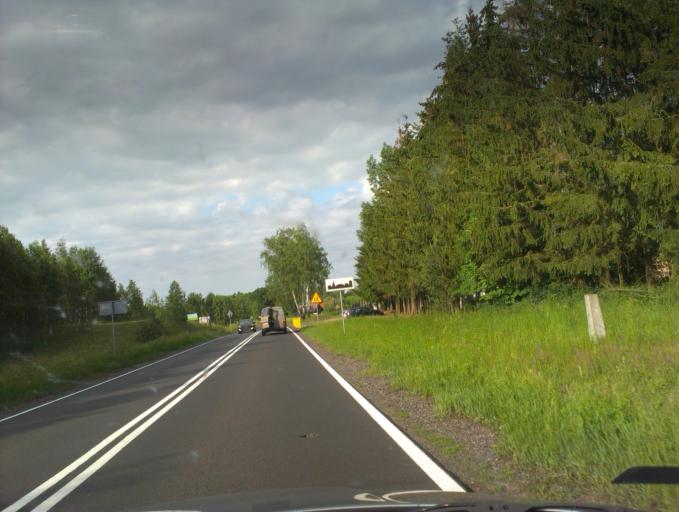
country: PL
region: West Pomeranian Voivodeship
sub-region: Powiat szczecinecki
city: Borne Sulinowo
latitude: 53.6213
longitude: 16.5978
